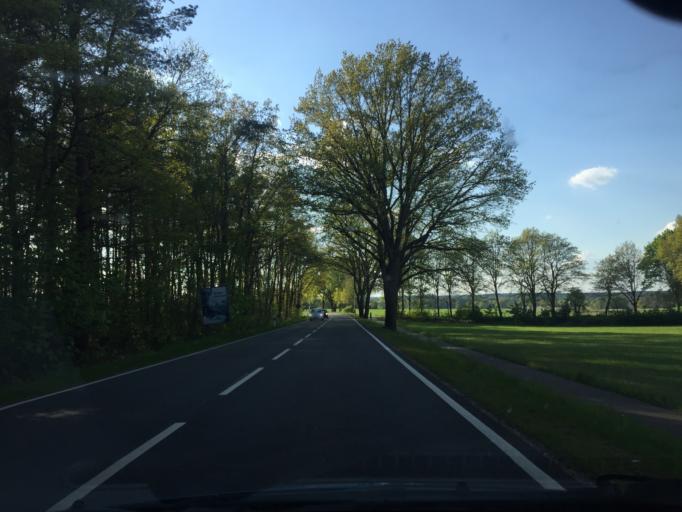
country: DE
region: Lower Saxony
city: Karwitz
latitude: 53.1260
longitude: 10.9770
